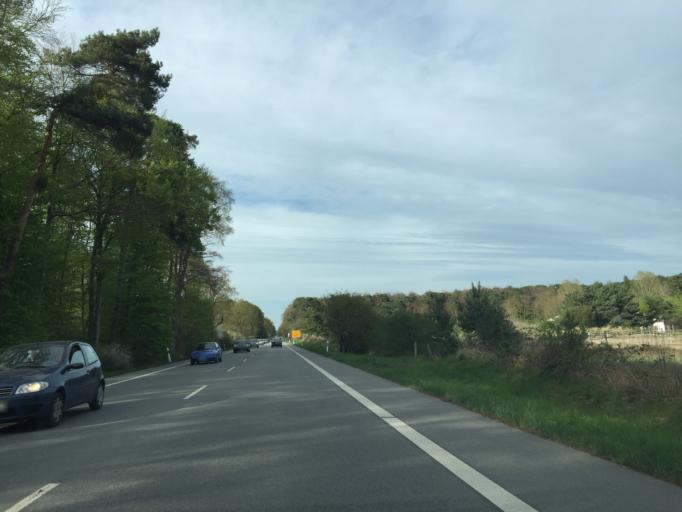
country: DE
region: Hesse
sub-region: Regierungsbezirk Darmstadt
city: Bickenbach
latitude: 49.7719
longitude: 8.6254
